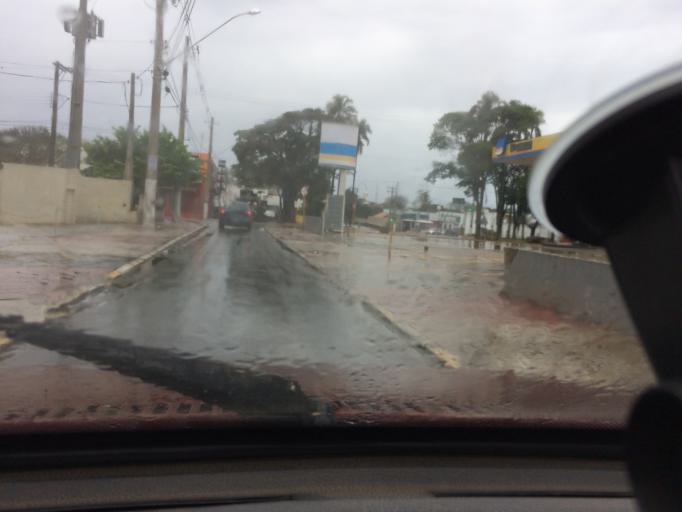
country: BR
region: Sao Paulo
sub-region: Capao Bonito
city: Capao Bonito
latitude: -24.0058
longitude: -48.3461
